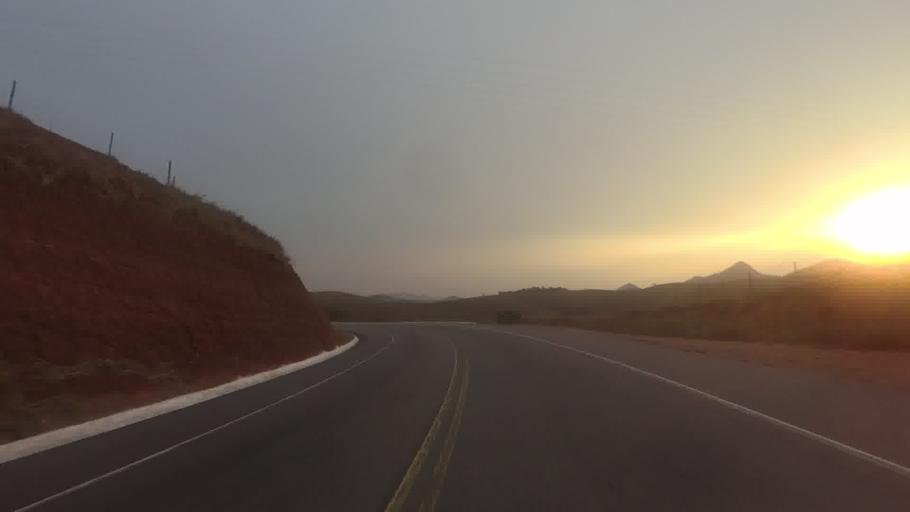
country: BR
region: Minas Gerais
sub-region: Recreio
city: Recreio
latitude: -21.7228
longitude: -42.4430
